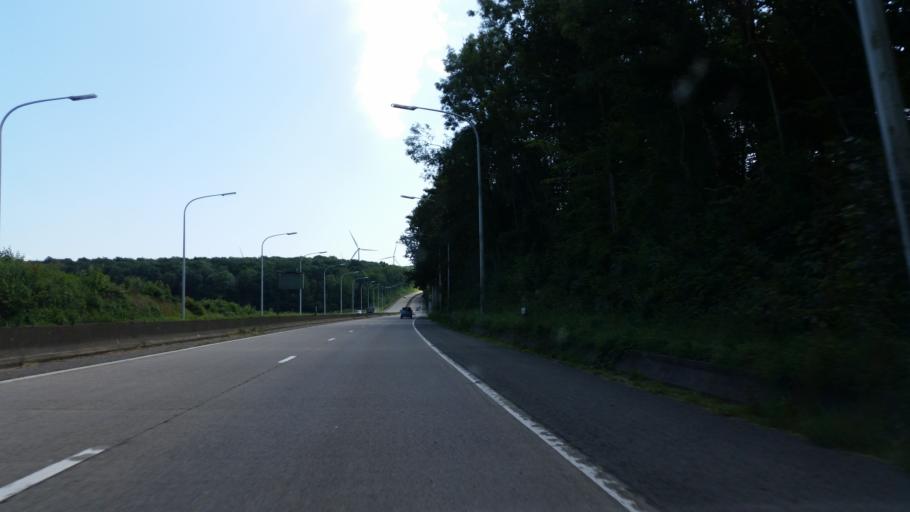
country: BE
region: Wallonia
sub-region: Province de Namur
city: Hamois
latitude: 50.3073
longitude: 5.1566
